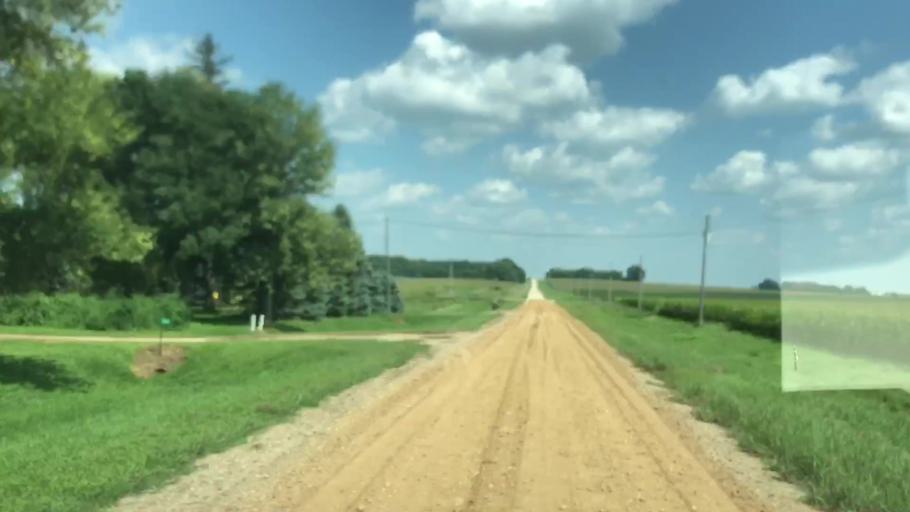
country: US
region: Iowa
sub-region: O'Brien County
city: Sheldon
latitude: 43.1568
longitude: -95.7869
